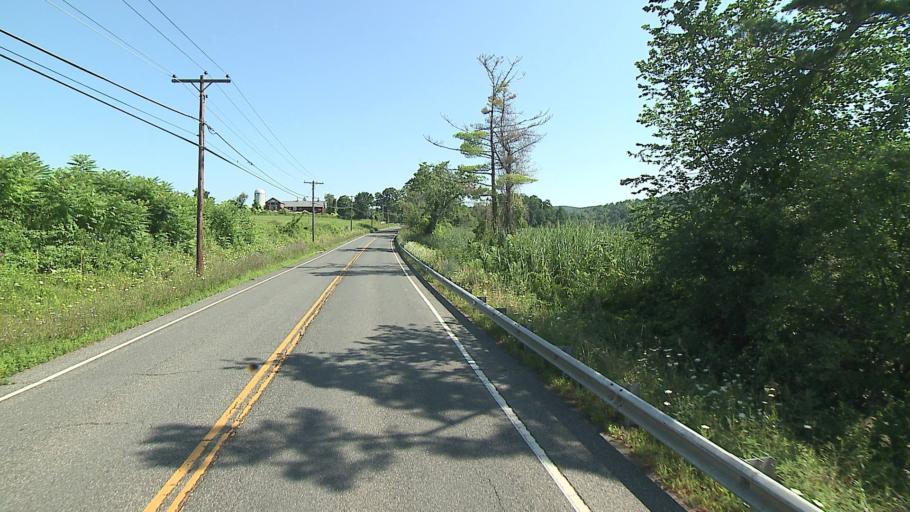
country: US
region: Connecticut
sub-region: Litchfield County
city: Kent
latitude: 41.8960
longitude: -73.4505
